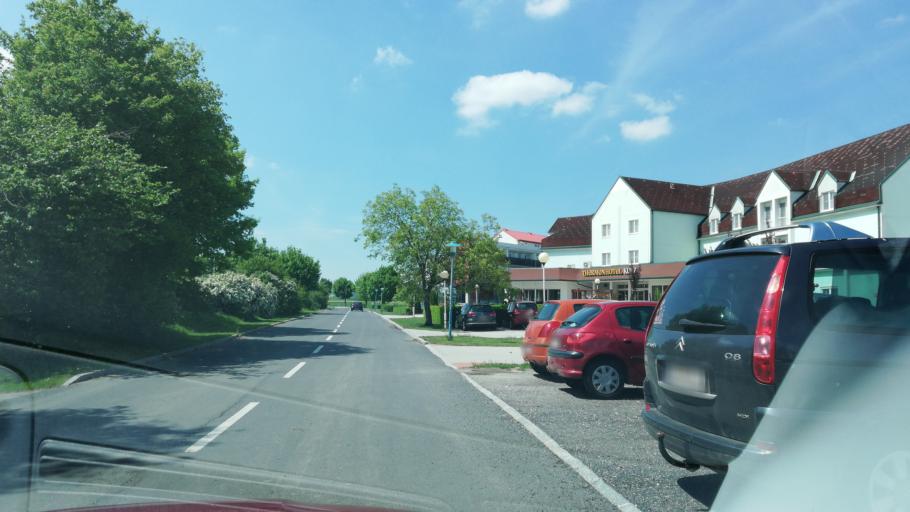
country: AT
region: Burgenland
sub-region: Politischer Bezirk Oberpullendorf
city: Lutzmannsburg
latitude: 47.4657
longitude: 16.6598
